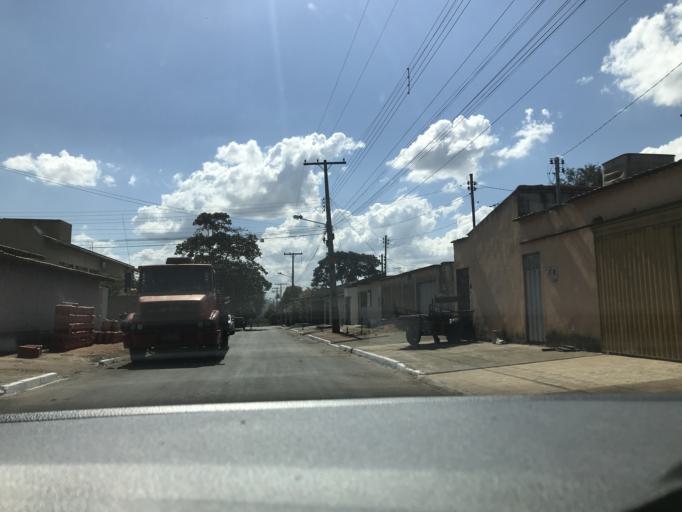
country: BR
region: Goias
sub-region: Senador Canedo
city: Senador Canedo
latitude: -16.6511
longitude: -49.1530
